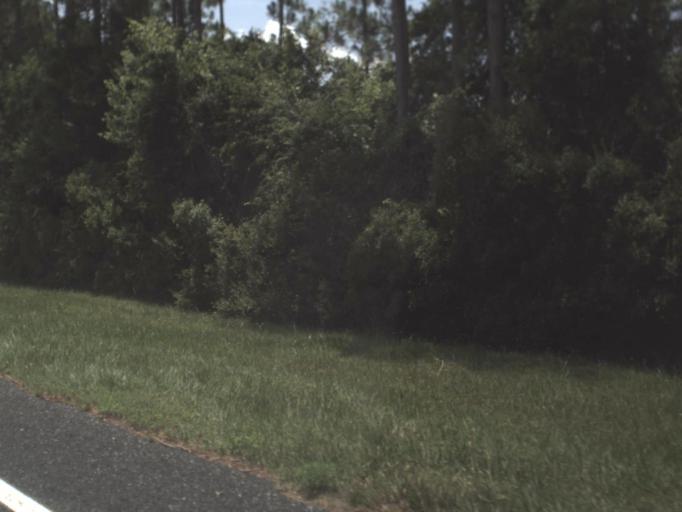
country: US
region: Florida
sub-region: Taylor County
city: Steinhatchee
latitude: 29.7133
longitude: -83.2993
